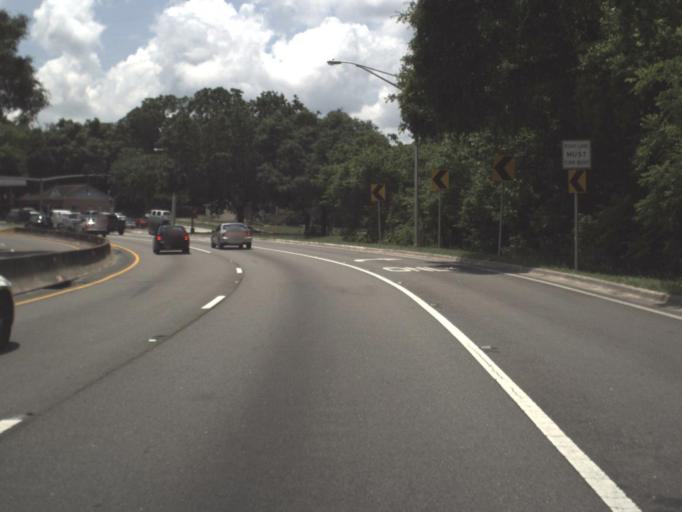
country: US
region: Florida
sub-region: Duval County
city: Jacksonville
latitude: 30.2931
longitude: -81.7237
